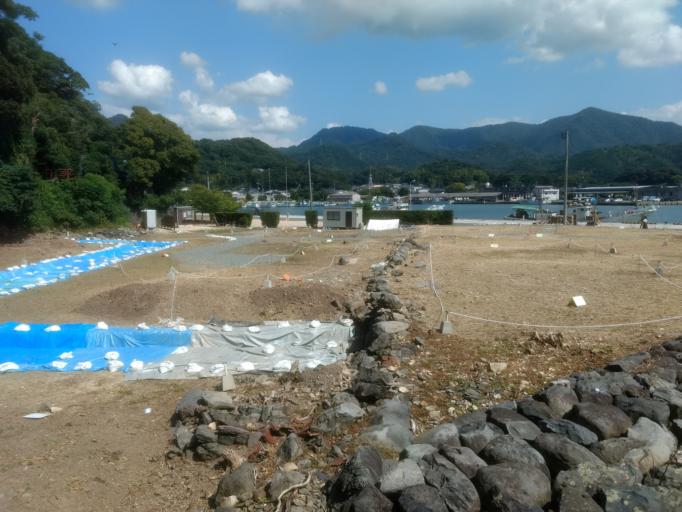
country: JP
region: Yamaguchi
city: Hagi
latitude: 34.4306
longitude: 131.4116
